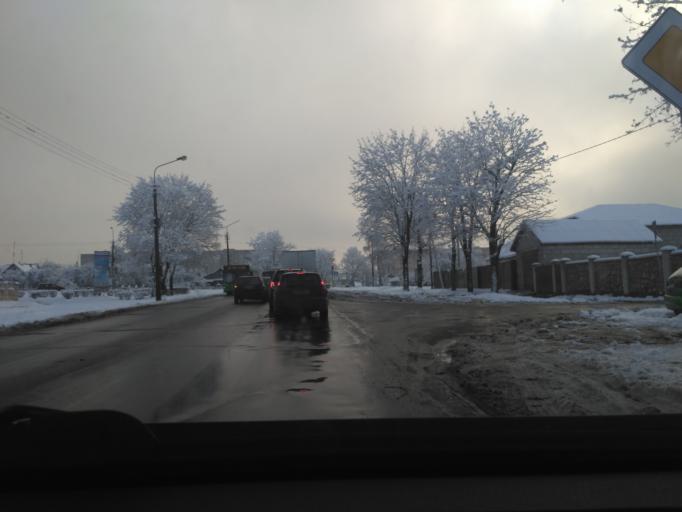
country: BY
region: Minsk
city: Horad Barysaw
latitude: 54.2271
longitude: 28.4946
